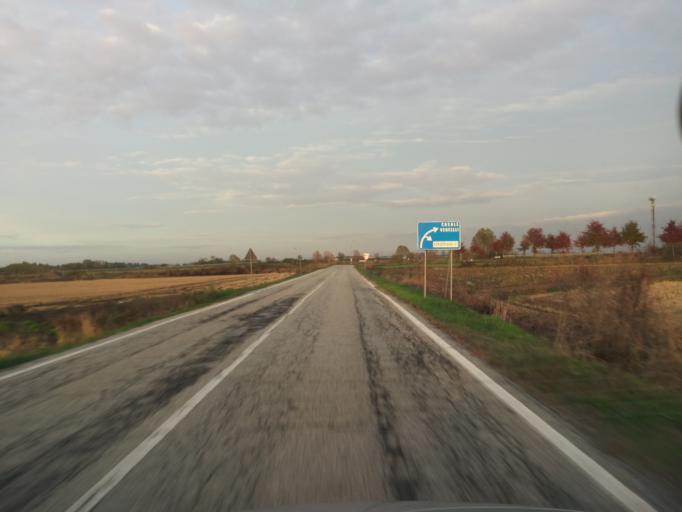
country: IT
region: Piedmont
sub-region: Provincia di Vercelli
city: Stroppiana
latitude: 45.2370
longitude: 8.4547
